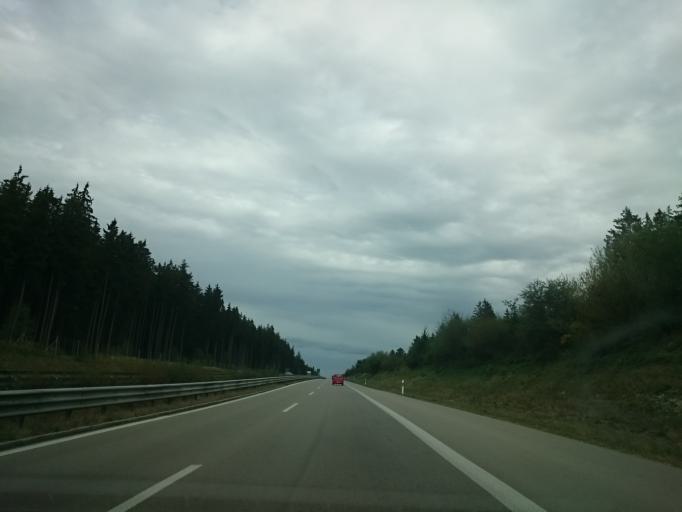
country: DE
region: Bavaria
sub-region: Upper Bavaria
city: Hurlach
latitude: 48.0919
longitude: 10.8382
